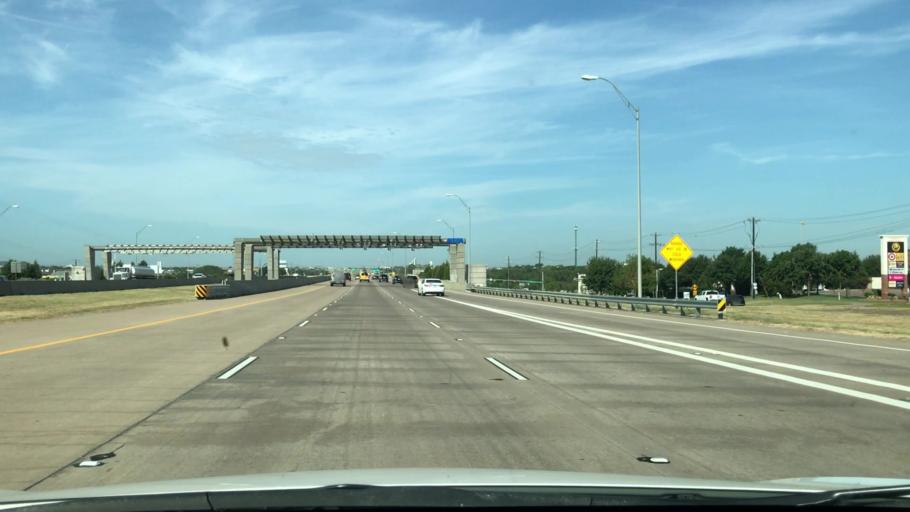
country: US
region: Texas
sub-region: Collin County
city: Allen
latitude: 33.1263
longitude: -96.7302
